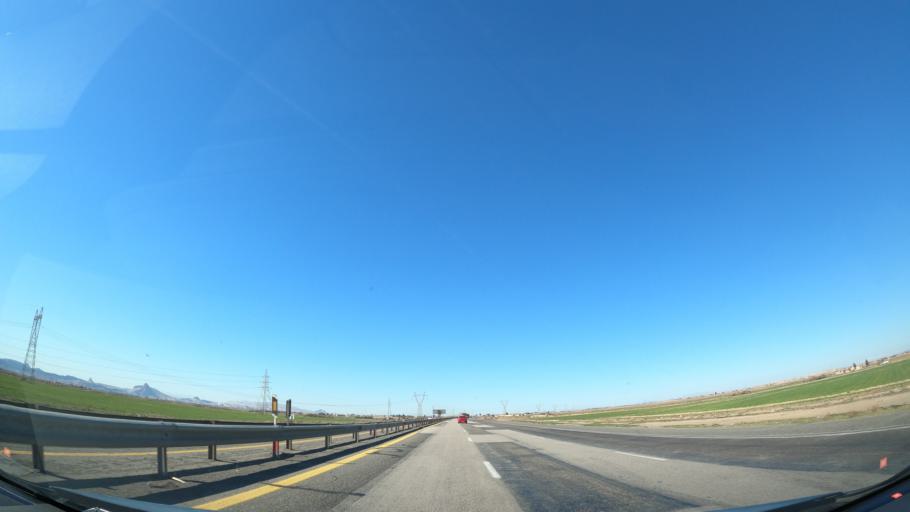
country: IR
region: Qom
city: Qom
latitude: 34.5673
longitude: 50.9876
